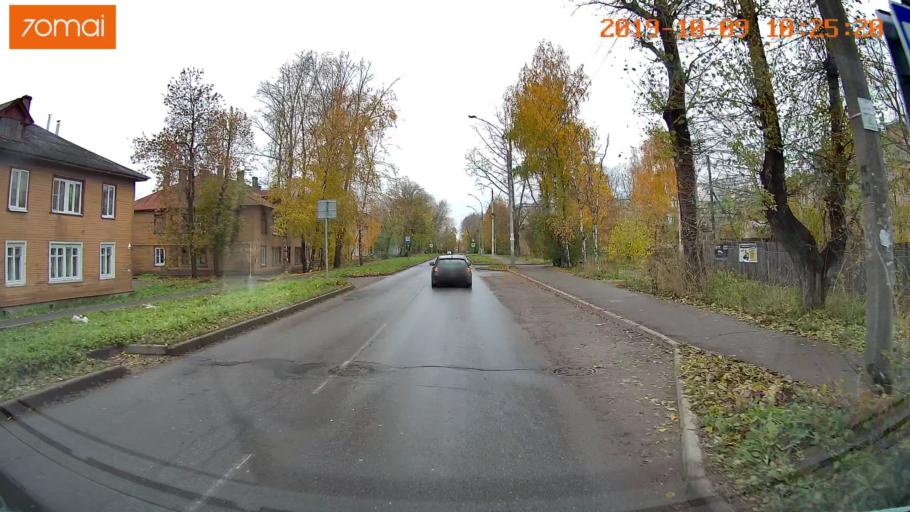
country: RU
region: Vologda
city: Vologda
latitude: 59.2130
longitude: 39.9308
